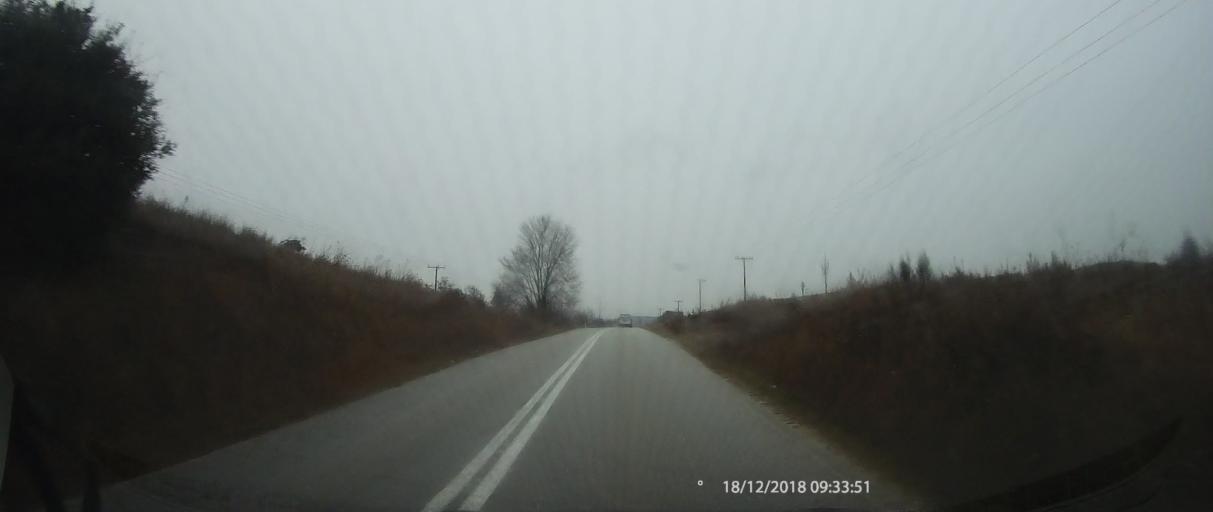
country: GR
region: Thessaly
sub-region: Nomos Larisis
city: Elassona
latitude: 39.9658
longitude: 22.1787
